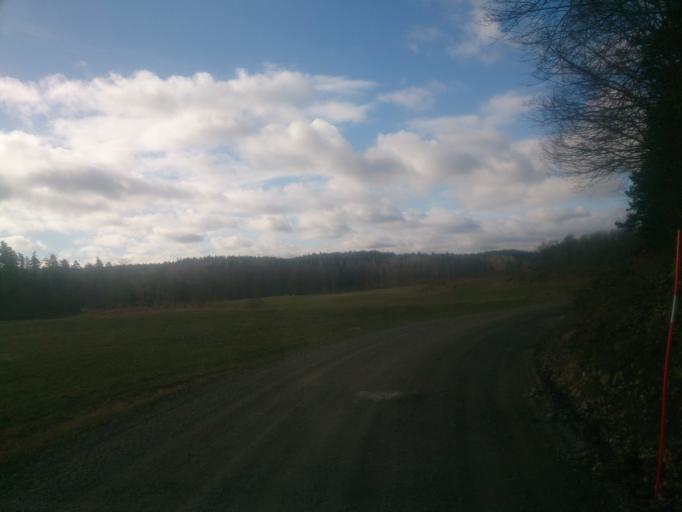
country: SE
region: OEstergoetland
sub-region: Atvidabergs Kommun
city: Atvidaberg
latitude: 58.2354
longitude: 16.1805
